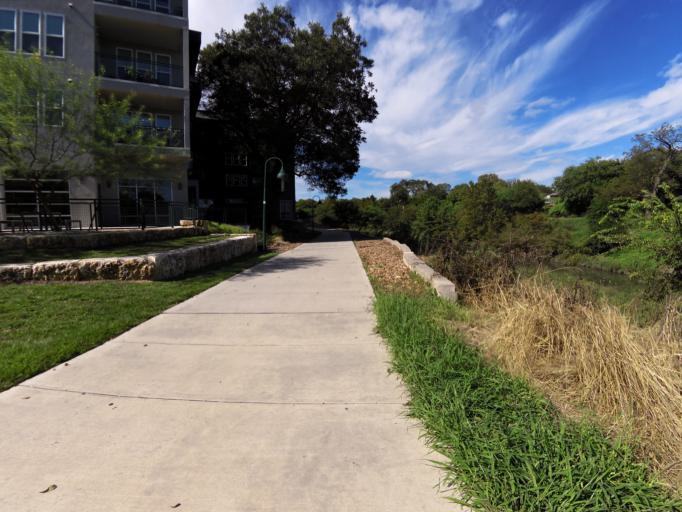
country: US
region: Texas
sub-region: Bexar County
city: San Antonio
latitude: 29.4053
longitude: -98.4918
